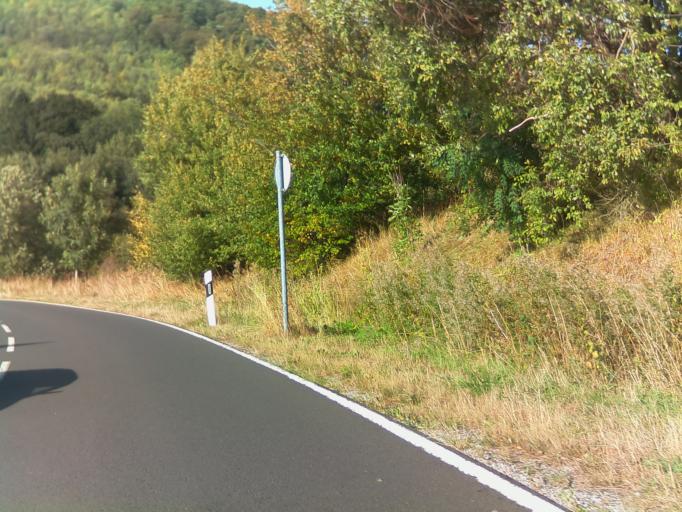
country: DE
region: Thuringia
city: Birx
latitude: 50.5223
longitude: 10.0386
